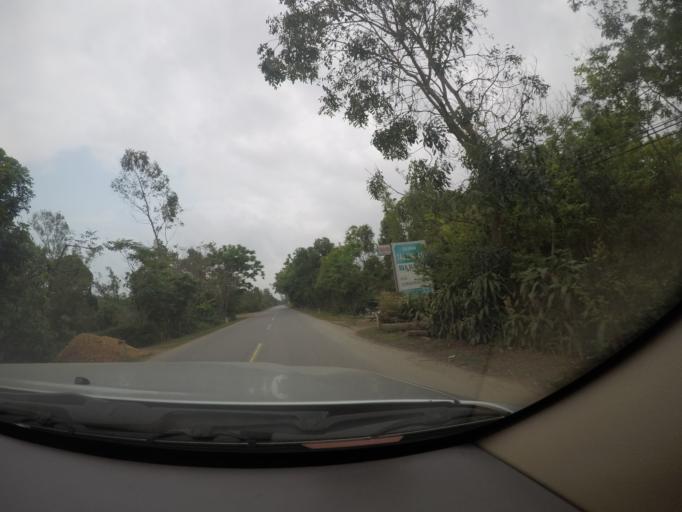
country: VN
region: Quang Binh
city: Kien Giang
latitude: 17.2226
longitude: 106.7066
